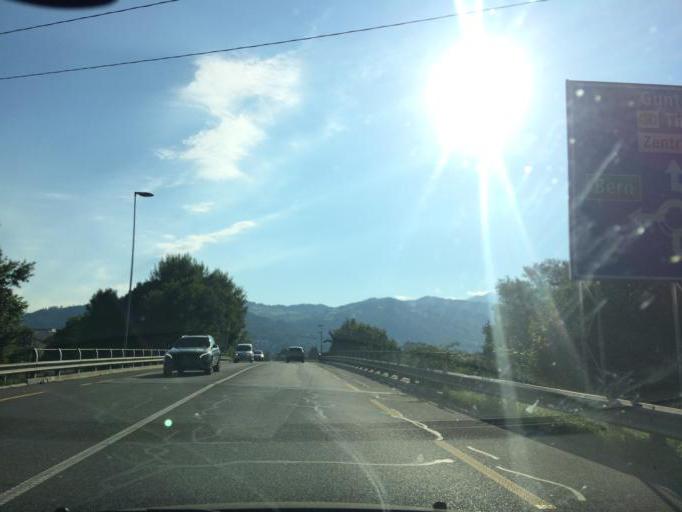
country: CH
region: Bern
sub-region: Thun District
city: Thun
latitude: 46.7424
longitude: 7.6019
